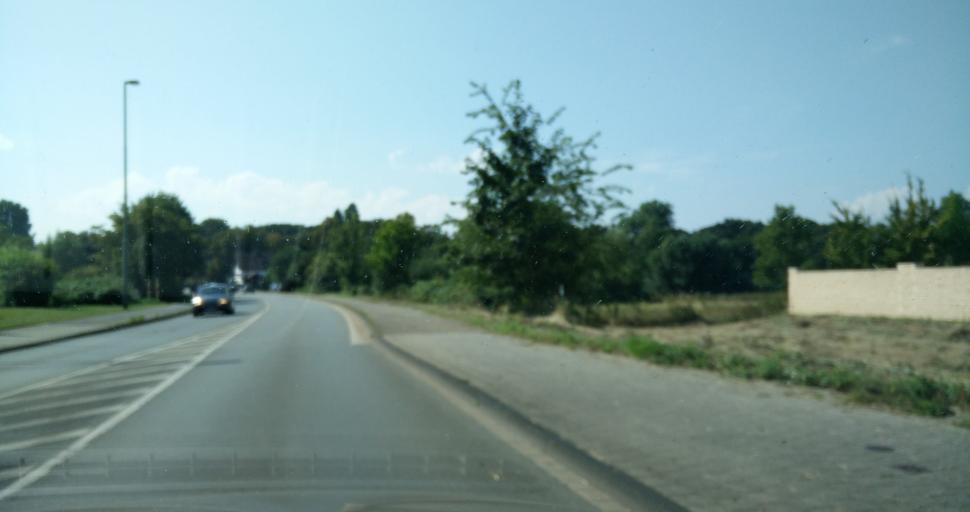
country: DE
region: North Rhine-Westphalia
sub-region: Regierungsbezirk Dusseldorf
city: Hochfeld
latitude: 51.3571
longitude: 6.7447
